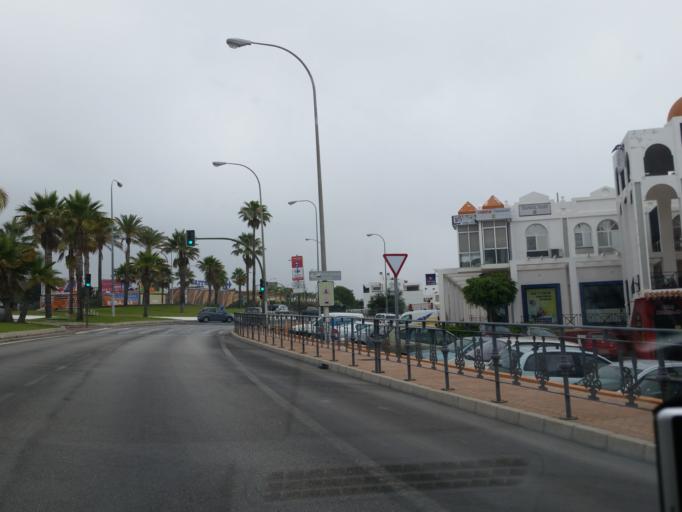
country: ES
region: Andalusia
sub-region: Provincia de Malaga
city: Torremolinos
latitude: 36.6085
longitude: -4.5139
